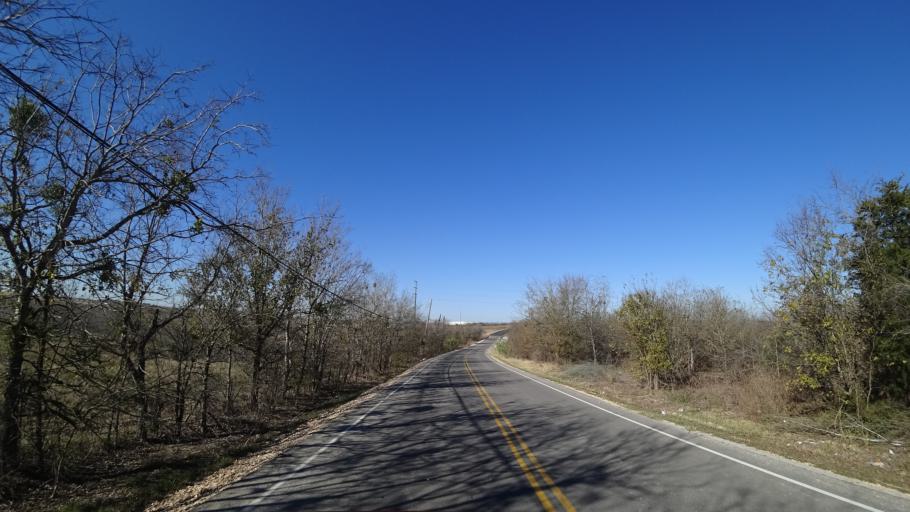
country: US
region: Texas
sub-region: Travis County
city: Garfield
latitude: 30.1155
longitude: -97.6550
